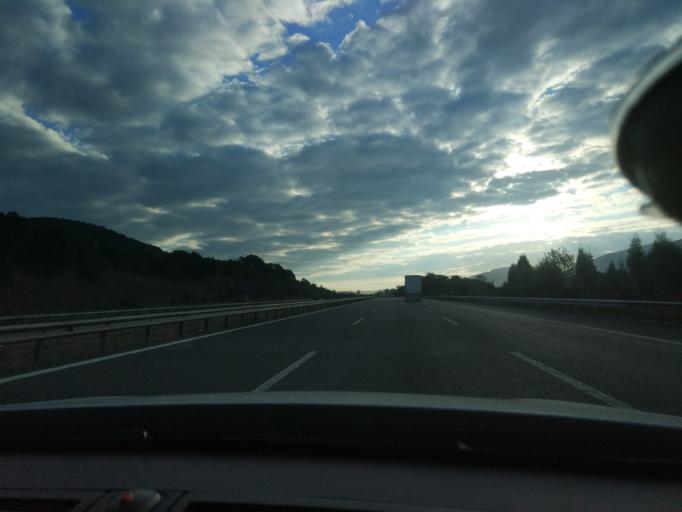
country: TR
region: Duzce
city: Gumusova
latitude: 40.8075
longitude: 30.8718
